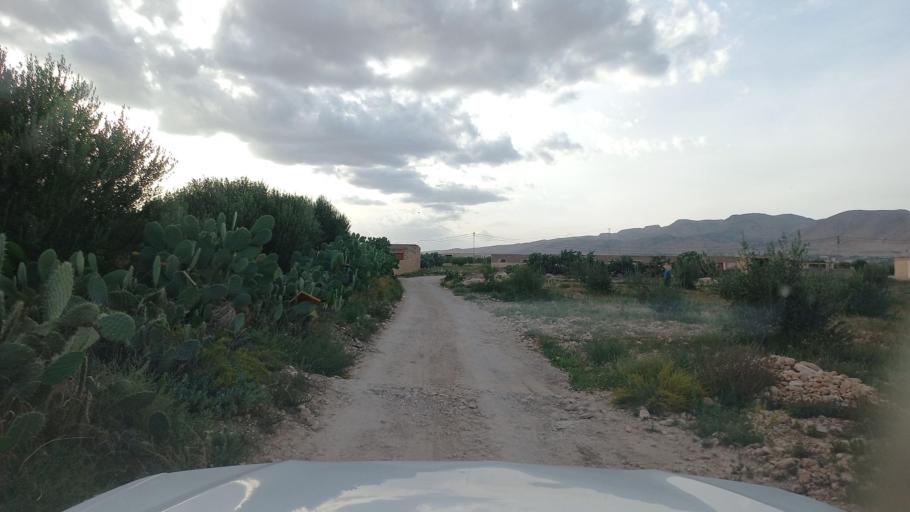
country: TN
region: Al Qasrayn
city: Sbiba
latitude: 35.4363
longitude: 9.0958
